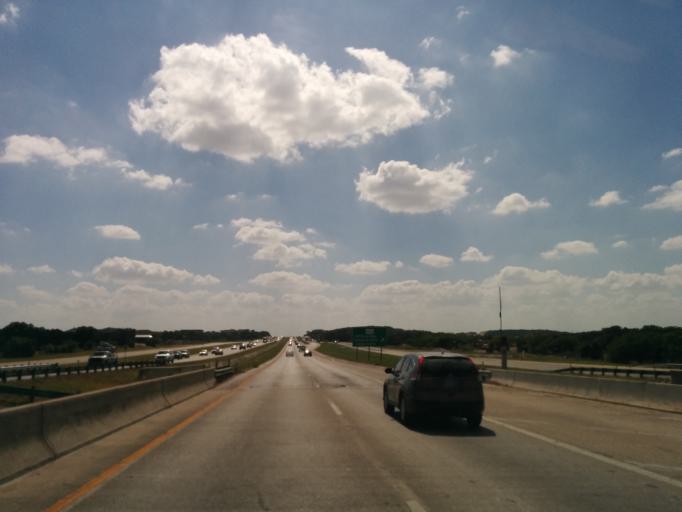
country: US
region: Texas
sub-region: Bexar County
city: Shavano Park
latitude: 29.6022
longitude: -98.5401
